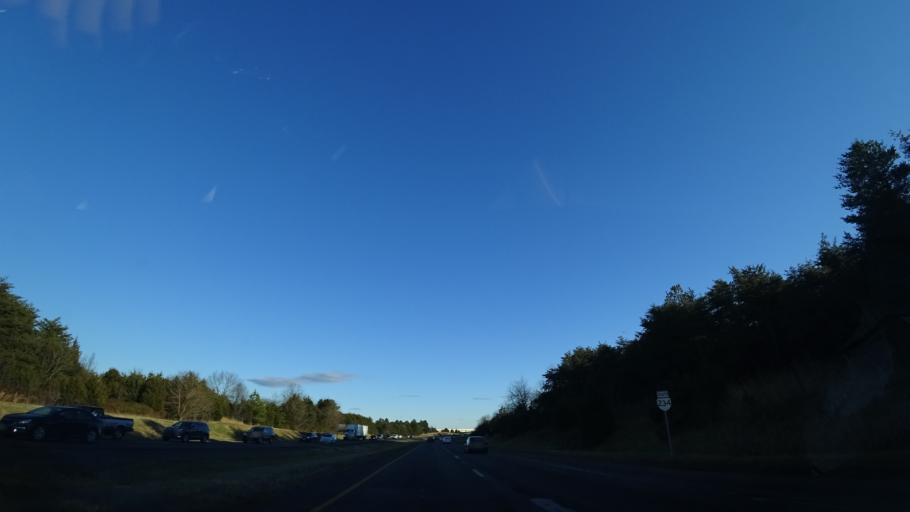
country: US
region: Virginia
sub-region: Prince William County
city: Linton Hall
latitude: 38.7914
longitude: -77.5569
